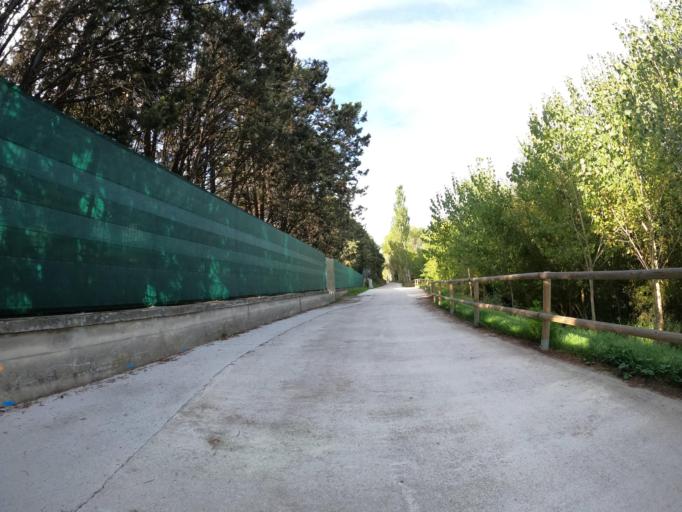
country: ES
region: Navarre
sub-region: Provincia de Navarra
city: Oltza
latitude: 42.8148
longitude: -1.7457
